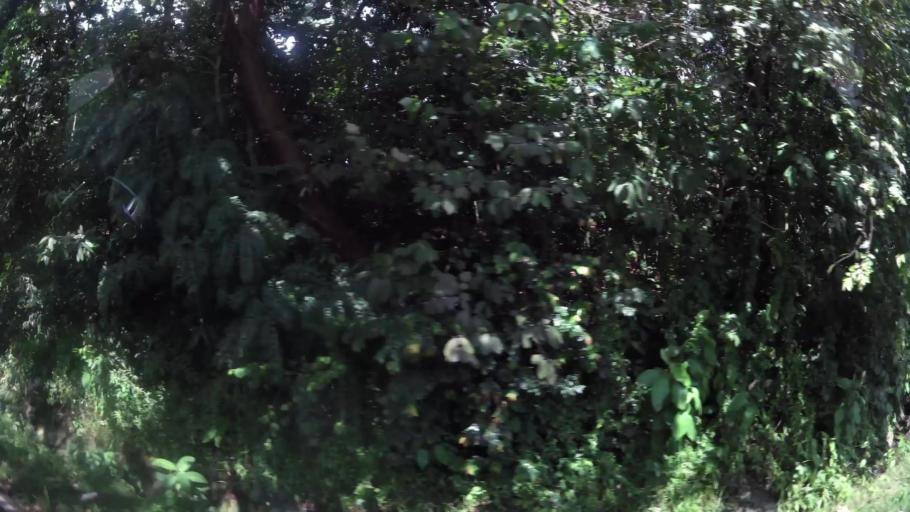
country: PA
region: Panama
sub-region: Distrito de Panama
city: Paraiso
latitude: 9.0342
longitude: -79.6253
